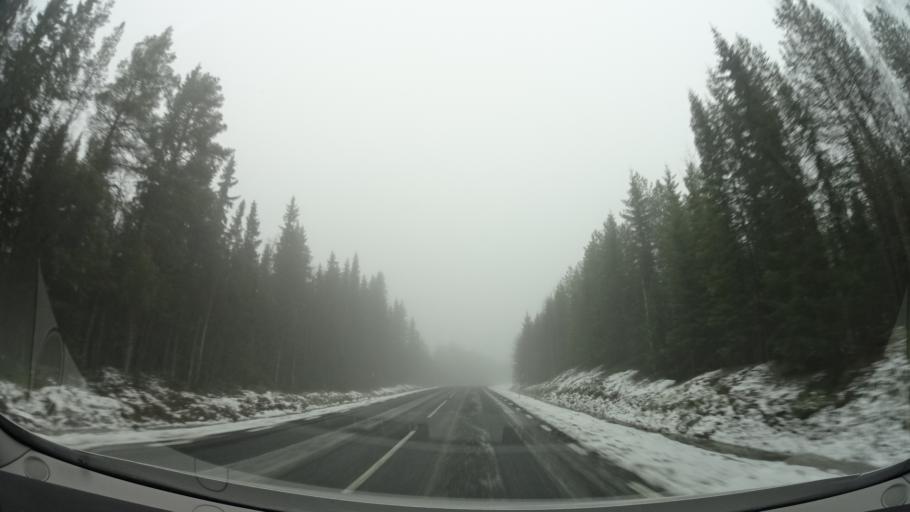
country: SE
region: Vaesterbotten
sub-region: Asele Kommun
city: Insjon
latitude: 64.2882
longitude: 17.6304
